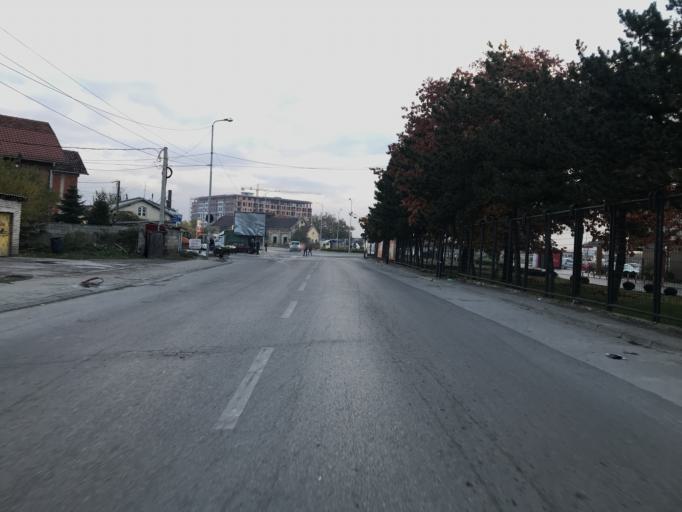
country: XK
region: Pec
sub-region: Komuna e Pejes
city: Peje
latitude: 42.6563
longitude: 20.3051
